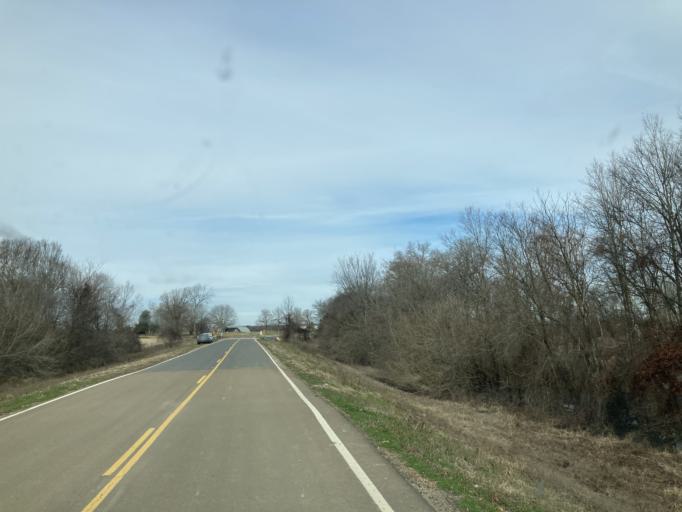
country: US
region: Mississippi
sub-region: Humphreys County
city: Belzoni
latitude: 33.1217
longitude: -90.6141
